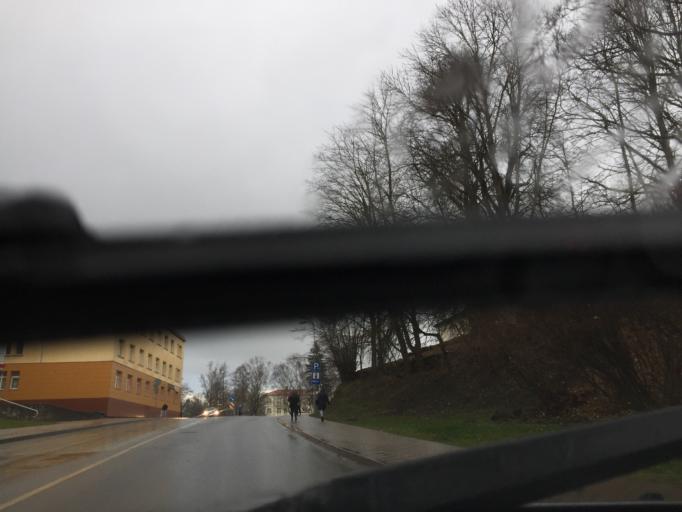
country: LV
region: Valmieras Rajons
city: Valmiera
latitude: 57.5370
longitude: 25.4234
